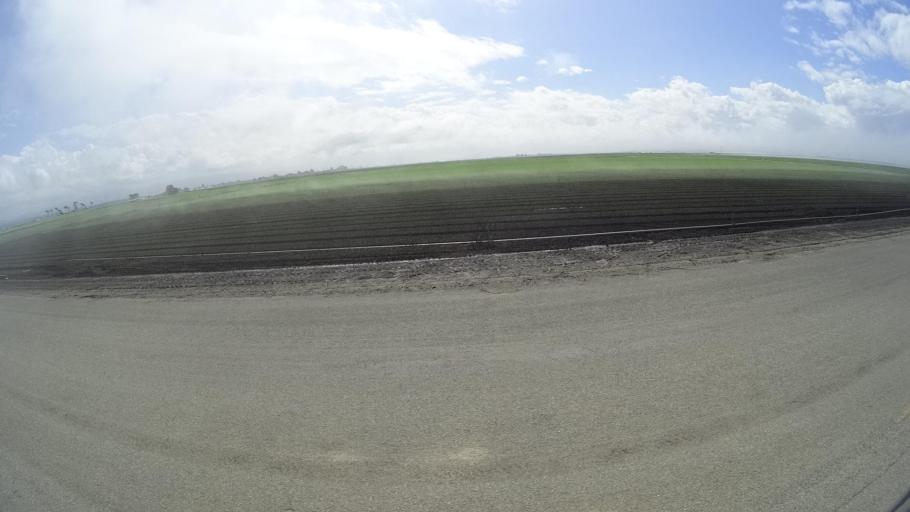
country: US
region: California
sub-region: Monterey County
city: Castroville
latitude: 36.7777
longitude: -121.7872
